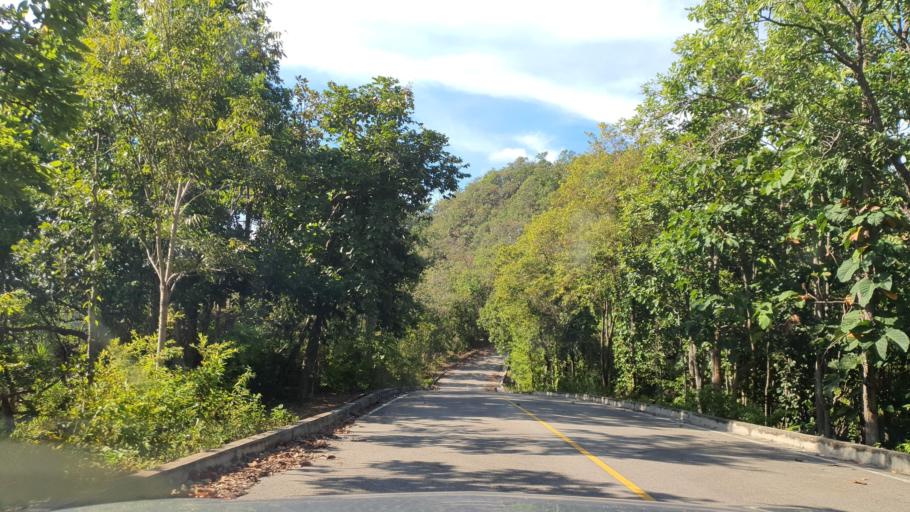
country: TH
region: Chiang Mai
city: Mae On
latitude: 18.7850
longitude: 99.2877
